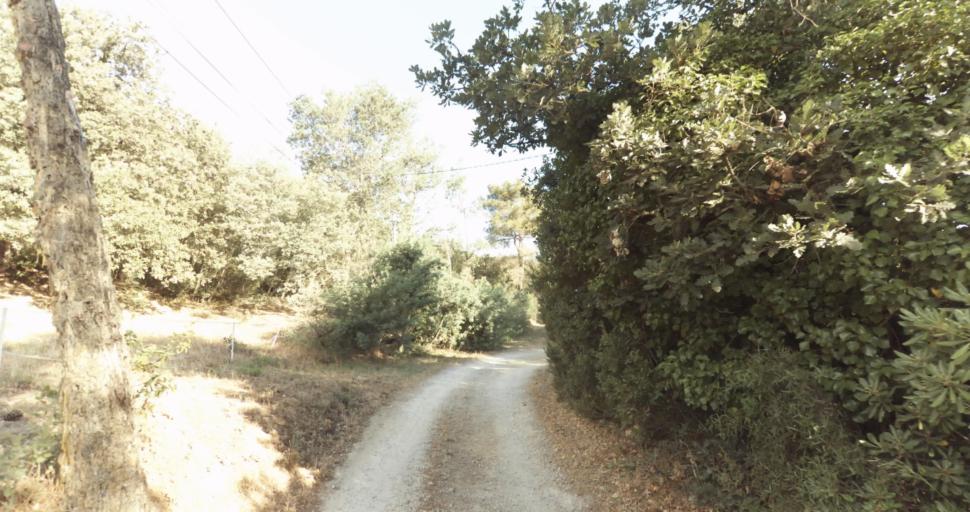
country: FR
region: Provence-Alpes-Cote d'Azur
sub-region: Departement du Var
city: Saint-Tropez
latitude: 43.2575
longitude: 6.6271
